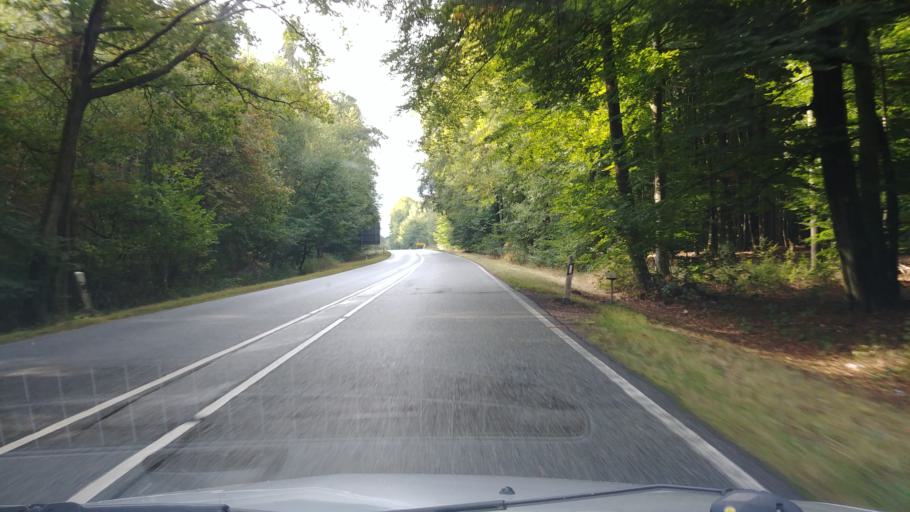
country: DE
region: Rheinland-Pfalz
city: Hochscheid
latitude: 49.9057
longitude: 7.2211
